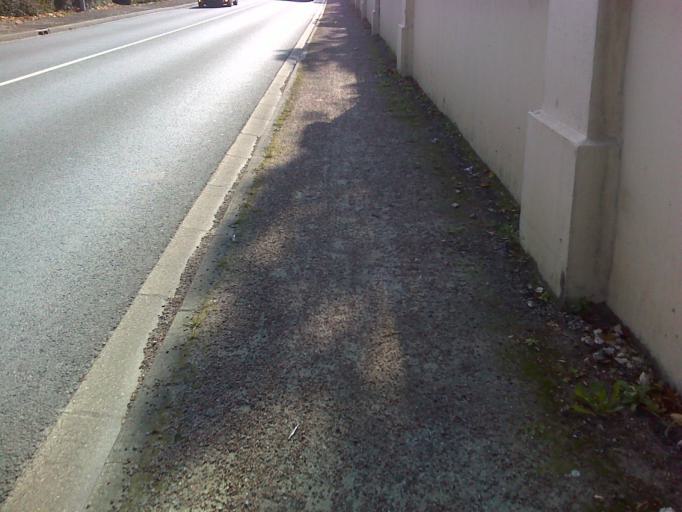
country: FR
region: Poitou-Charentes
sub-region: Departement de la Charente-Maritime
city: Rochefort
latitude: 45.9399
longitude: -0.9864
